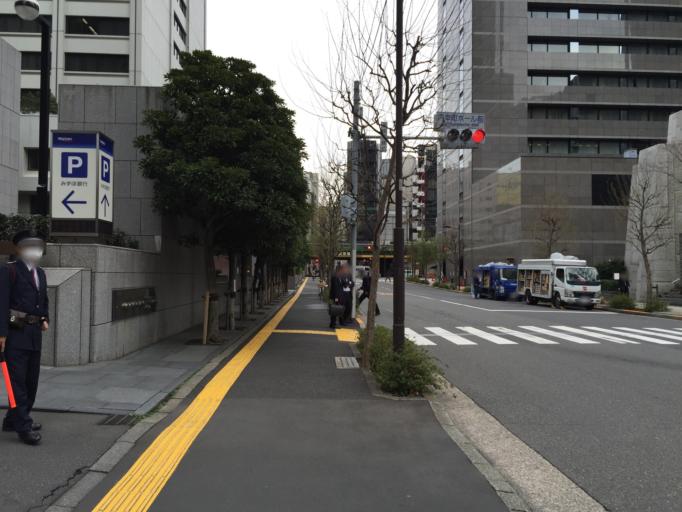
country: JP
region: Tokyo
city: Tokyo
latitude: 35.6702
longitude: 139.7575
